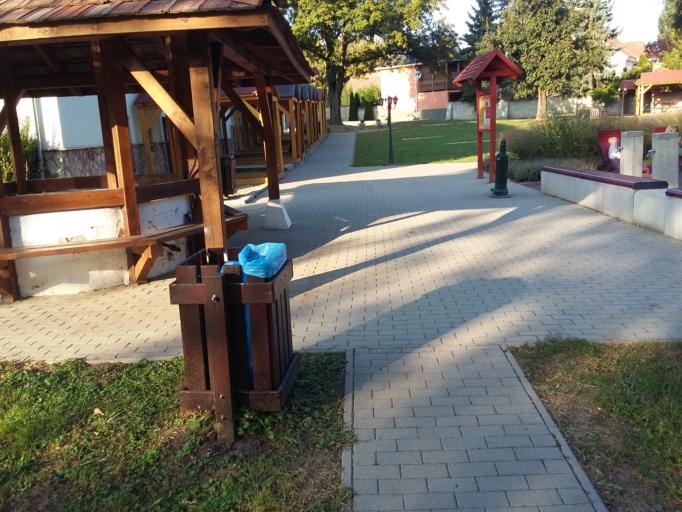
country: HU
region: Borsod-Abauj-Zemplen
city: Bekecs
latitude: 48.1511
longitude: 21.1719
